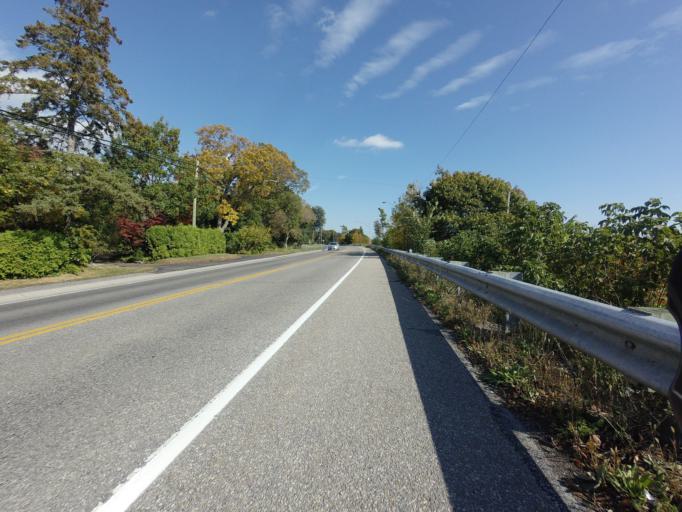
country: CA
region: Ontario
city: Kingston
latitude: 44.2177
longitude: -76.6484
